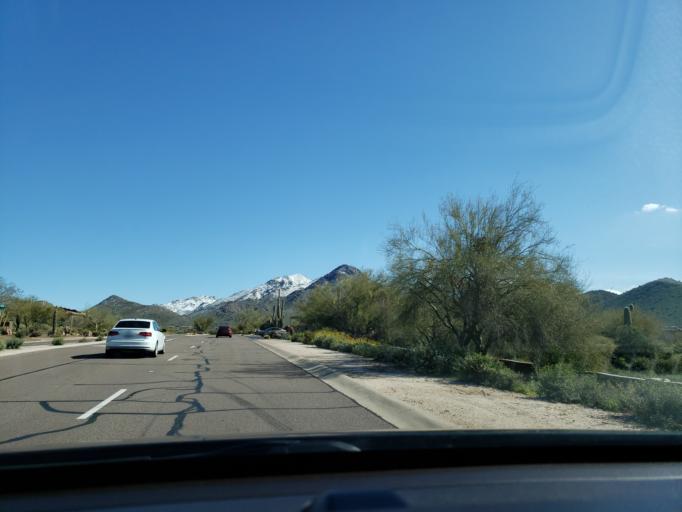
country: US
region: Arizona
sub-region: Maricopa County
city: Carefree
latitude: 33.7093
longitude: -111.8496
